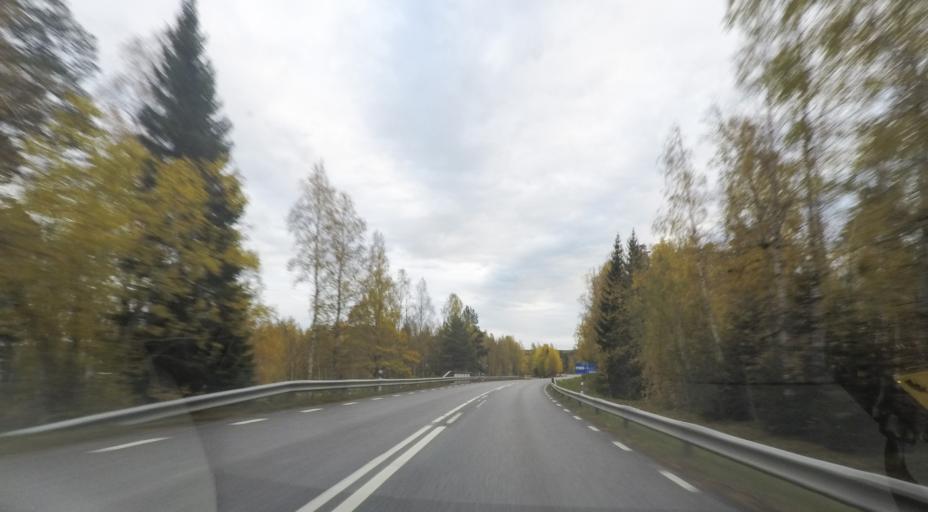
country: SE
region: OErebro
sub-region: Nora Kommun
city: As
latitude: 59.5124
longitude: 14.9634
